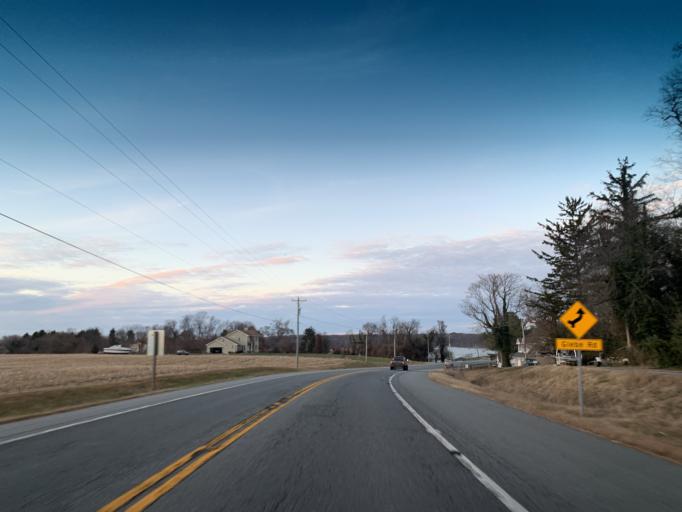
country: US
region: Maryland
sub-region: Cecil County
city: Elkton
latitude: 39.4570
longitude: -75.8711
